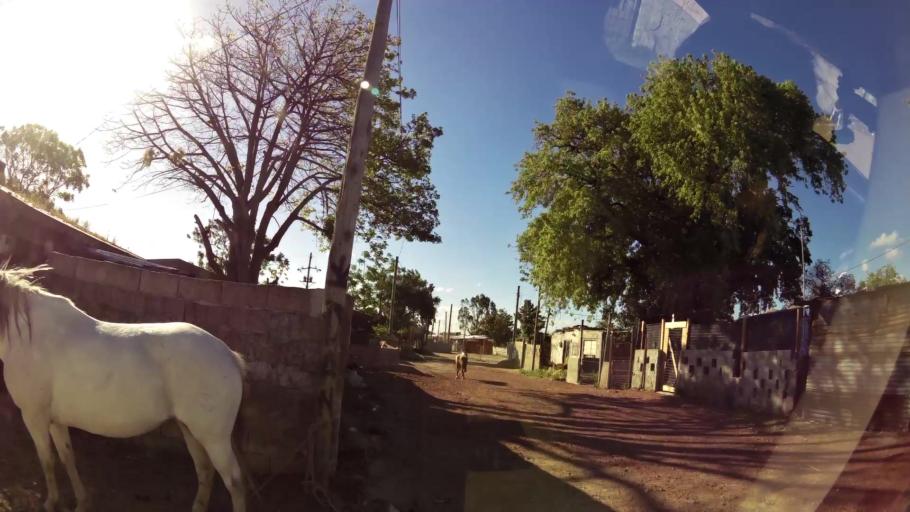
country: UY
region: Montevideo
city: Montevideo
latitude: -34.8430
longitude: -56.2332
